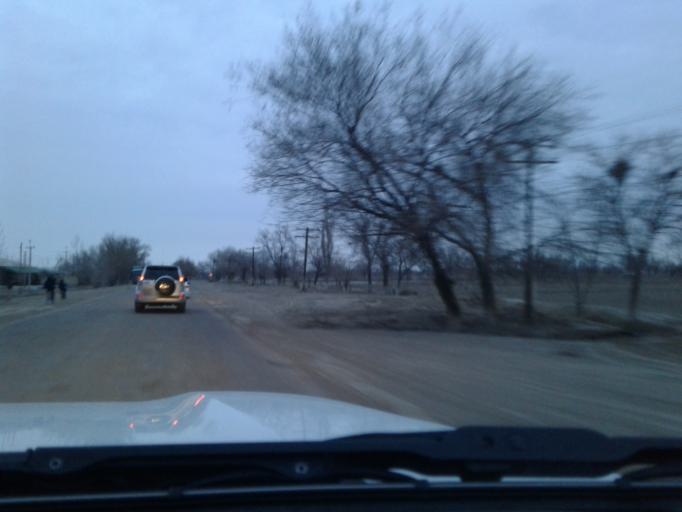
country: UZ
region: Karakalpakstan
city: Manghit
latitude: 42.0538
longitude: 59.9311
